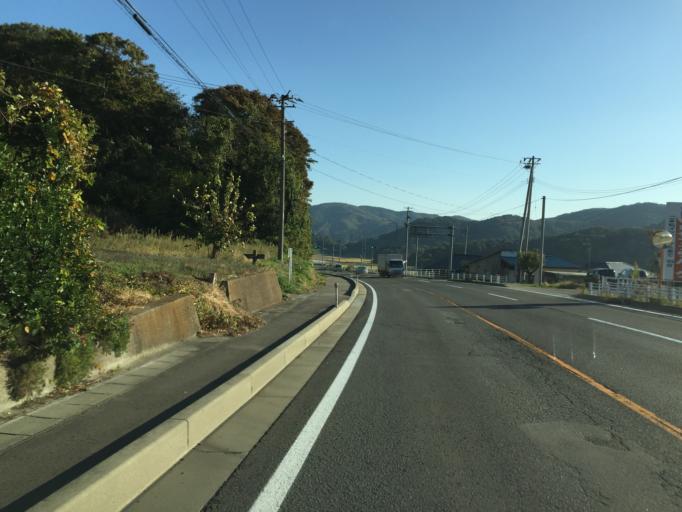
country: JP
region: Fukushima
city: Yanagawamachi-saiwaicho
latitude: 37.9125
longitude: 140.5892
